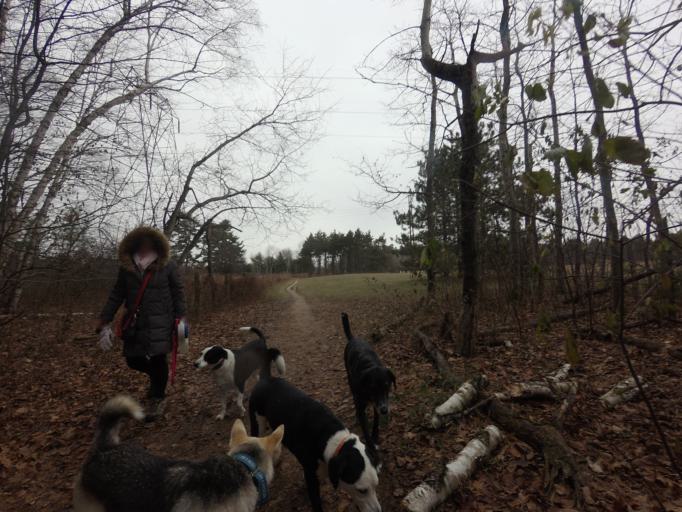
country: CA
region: Ontario
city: Bells Corners
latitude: 45.3223
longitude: -75.8021
